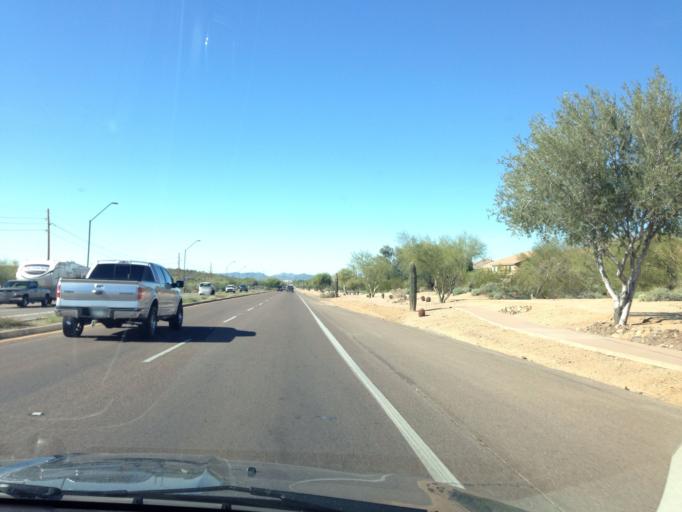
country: US
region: Arizona
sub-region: Maricopa County
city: Anthem
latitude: 33.7985
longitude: -112.1103
